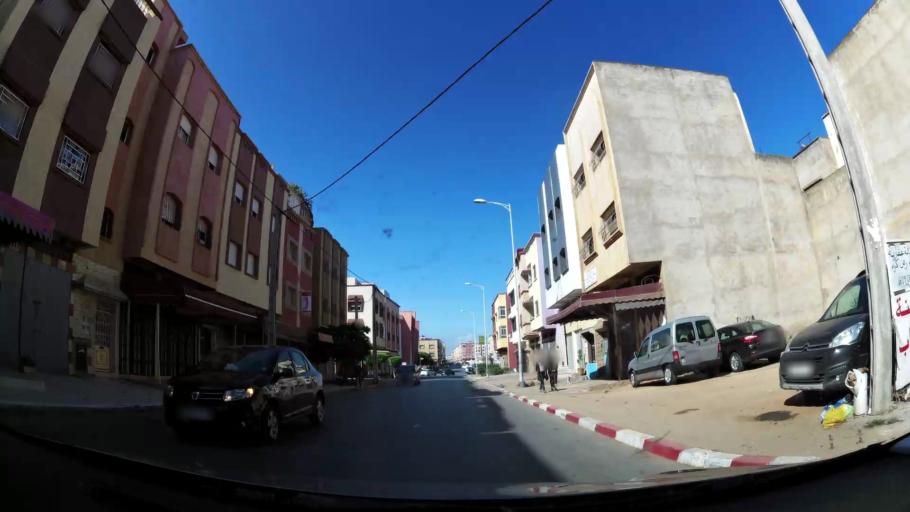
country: MA
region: Rabat-Sale-Zemmour-Zaer
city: Sale
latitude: 34.0712
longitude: -6.7968
